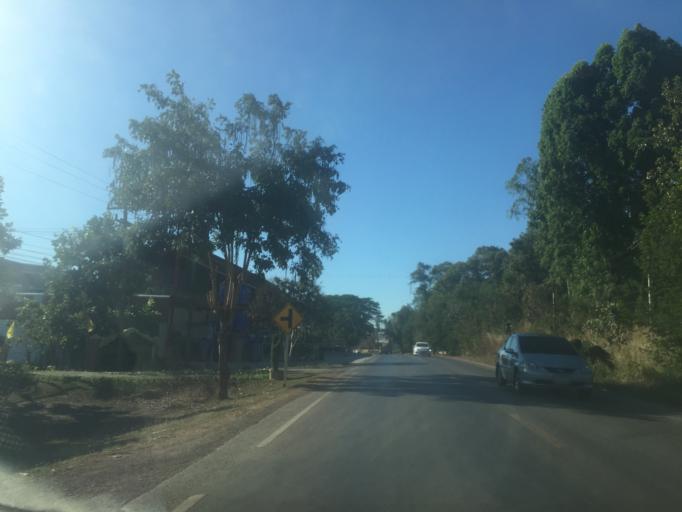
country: TH
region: Changwat Udon Thani
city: Si That
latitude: 16.9732
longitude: 103.2290
